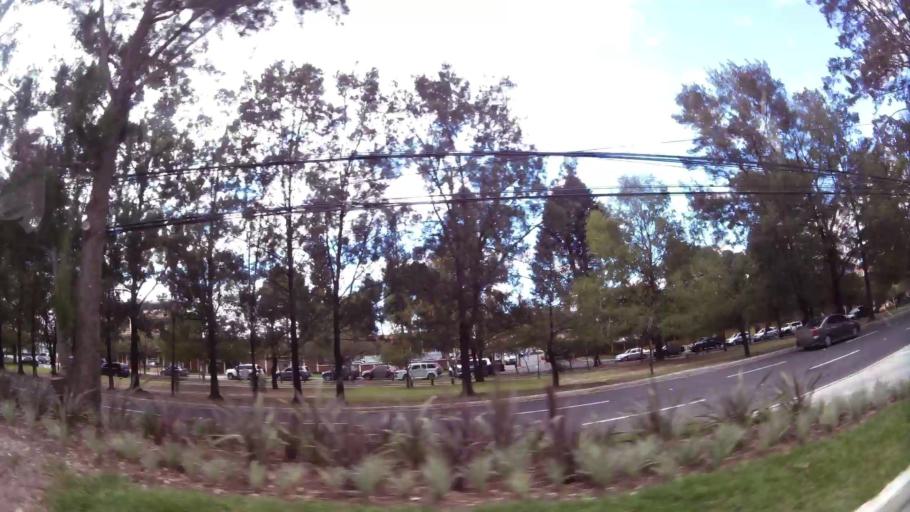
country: GT
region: Guatemala
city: Santa Catarina Pinula
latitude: 14.5876
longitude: -90.4892
